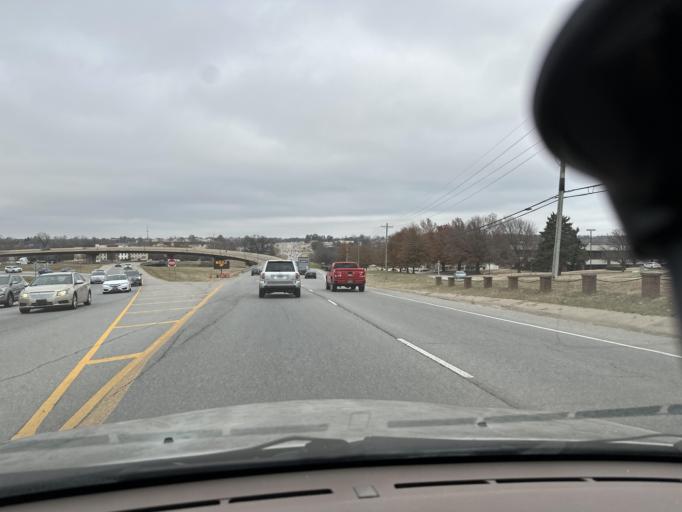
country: US
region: Arkansas
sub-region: Washington County
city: Johnson
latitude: 36.1150
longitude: -94.1450
